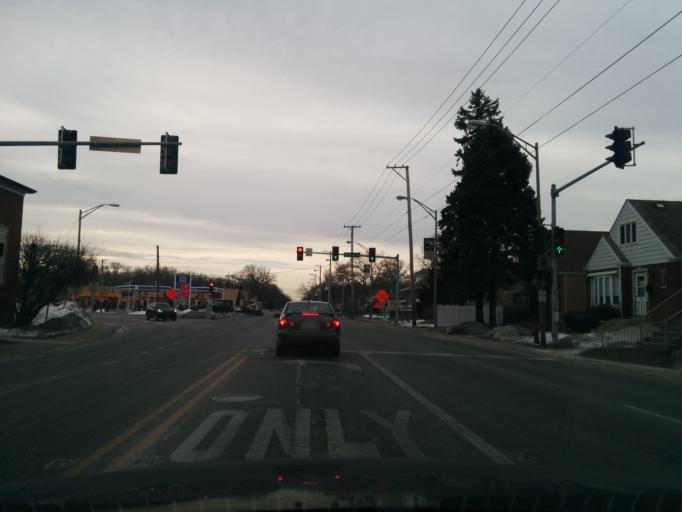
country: US
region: Illinois
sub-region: Cook County
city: River Grove
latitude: 41.9261
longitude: -87.8356
